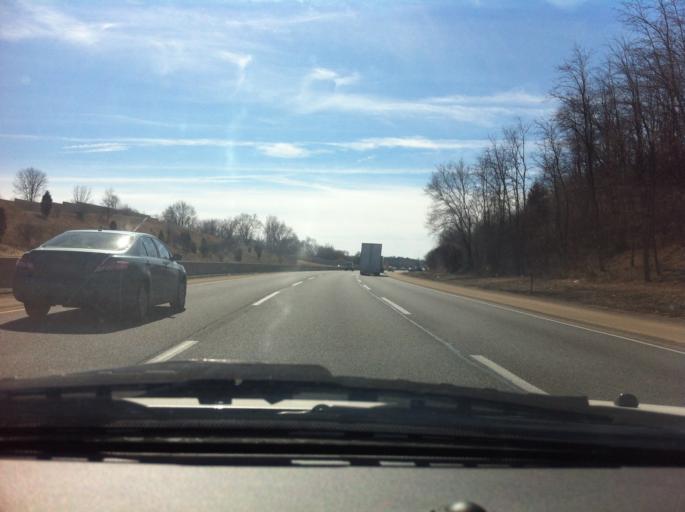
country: US
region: Wisconsin
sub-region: Rock County
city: Beloit
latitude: 42.4976
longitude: -88.9925
